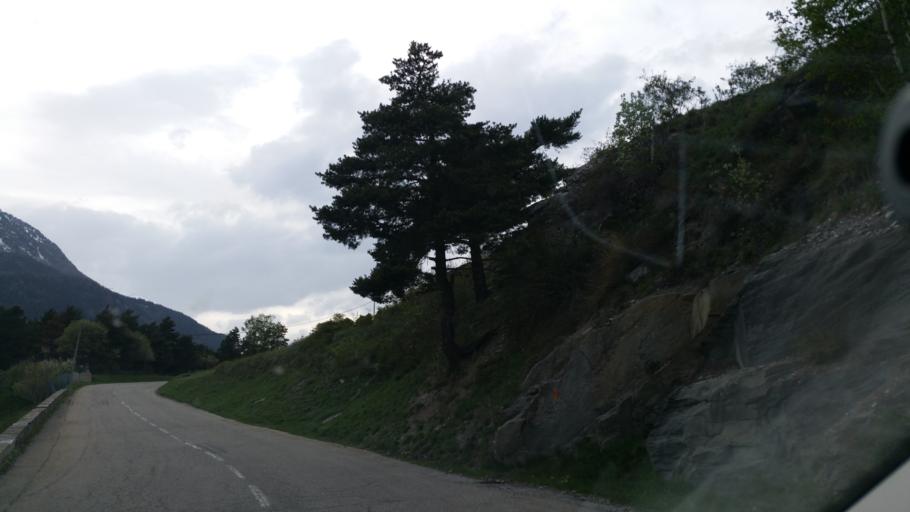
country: FR
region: Rhone-Alpes
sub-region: Departement de la Savoie
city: Modane
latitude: 45.2021
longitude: 6.6168
